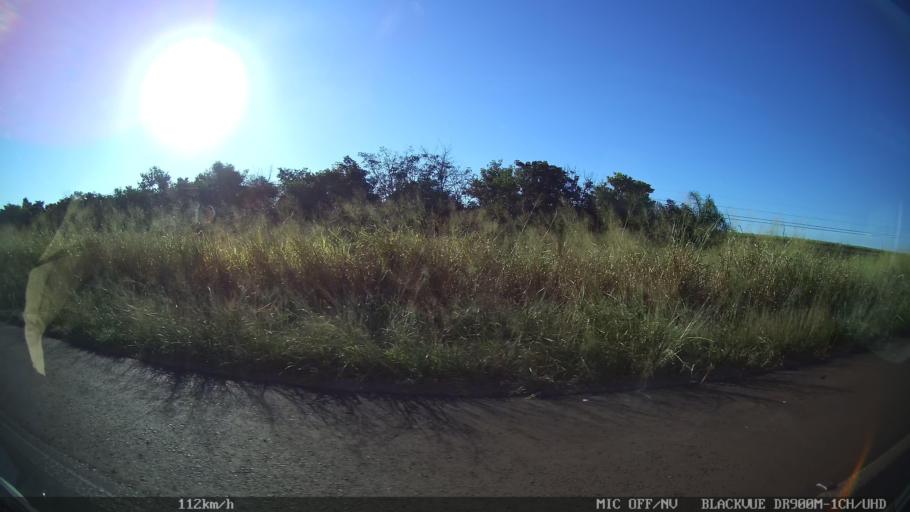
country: BR
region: Sao Paulo
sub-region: Guapiacu
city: Guapiacu
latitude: -20.7396
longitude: -49.0916
